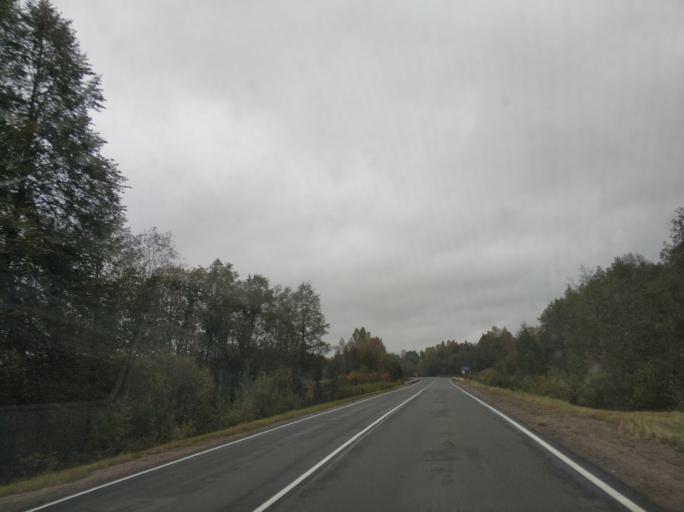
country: BY
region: Vitebsk
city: Rasony
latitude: 56.0985
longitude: 28.7236
